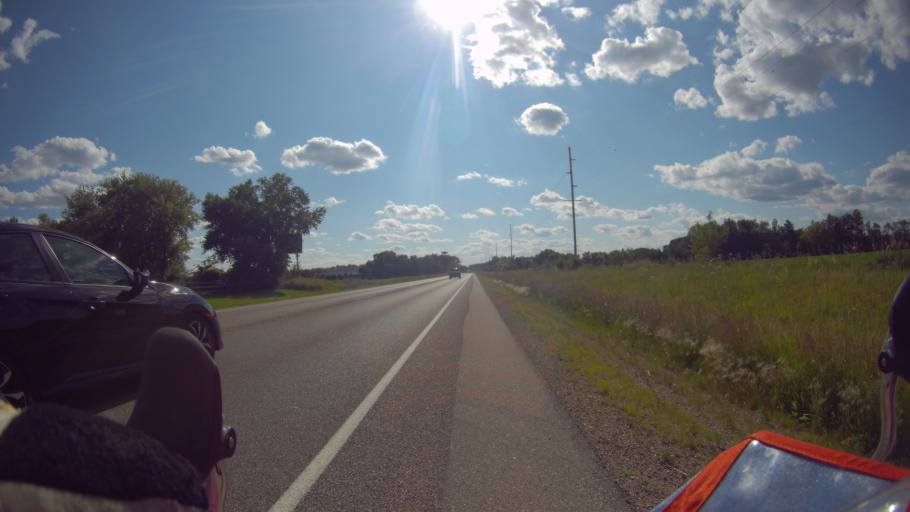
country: US
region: Wisconsin
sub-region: Dane County
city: Stoughton
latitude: 42.9190
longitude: -89.2949
